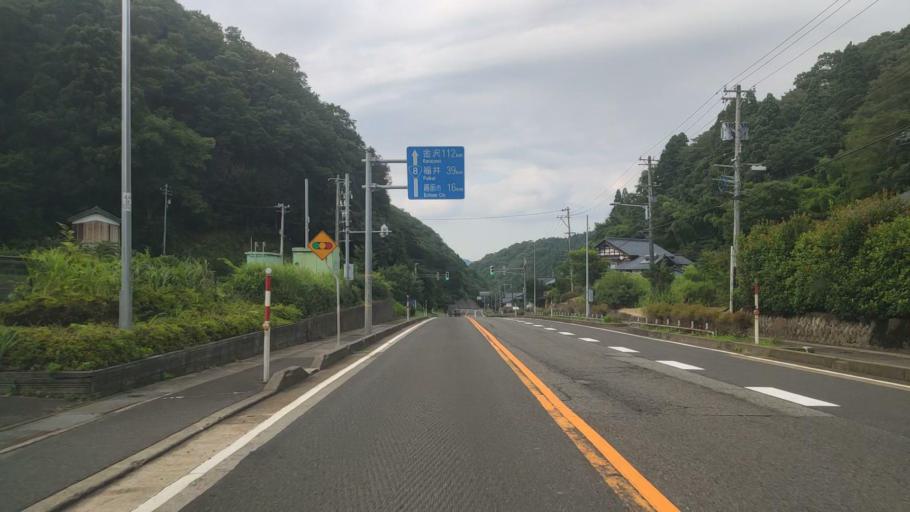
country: JP
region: Fukui
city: Takefu
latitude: 35.8002
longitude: 136.0915
